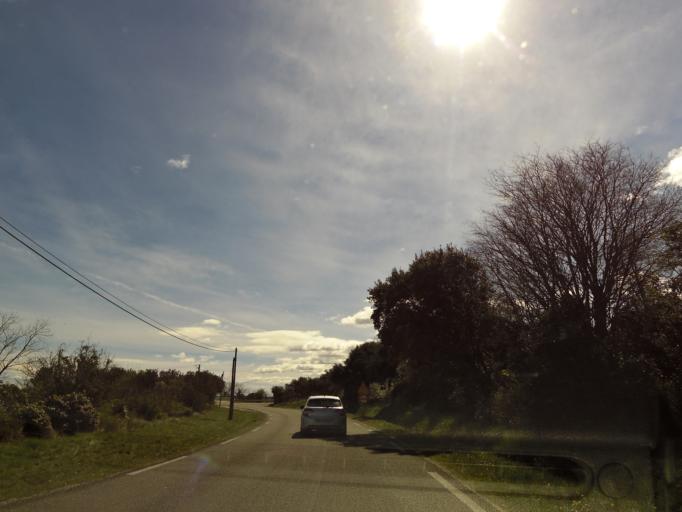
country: FR
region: Languedoc-Roussillon
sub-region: Departement du Gard
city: Bernis
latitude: 43.7761
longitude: 4.2826
